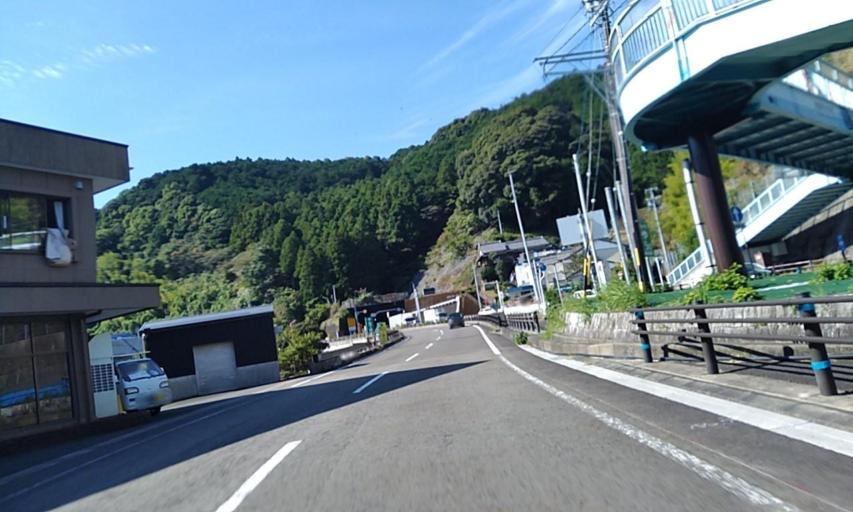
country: JP
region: Mie
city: Owase
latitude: 33.8959
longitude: 136.1161
